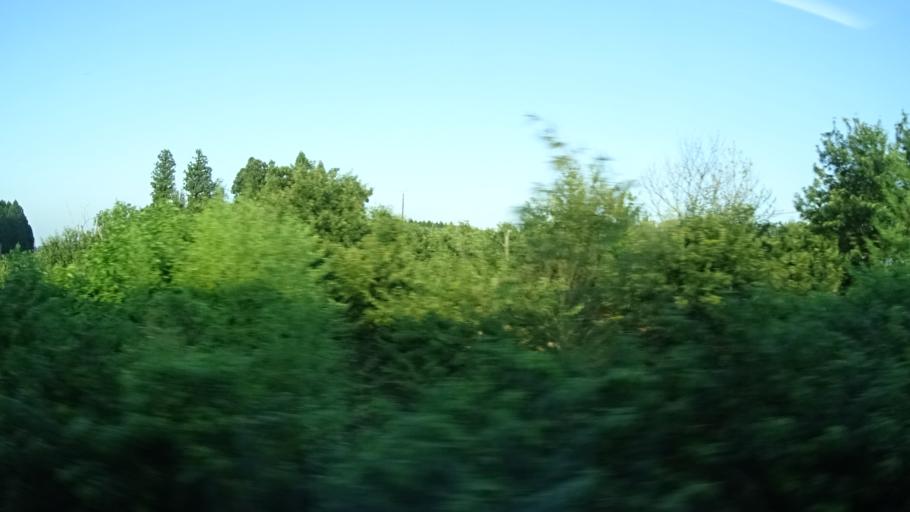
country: JP
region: Ibaraki
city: Tomobe
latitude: 36.3155
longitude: 140.2904
